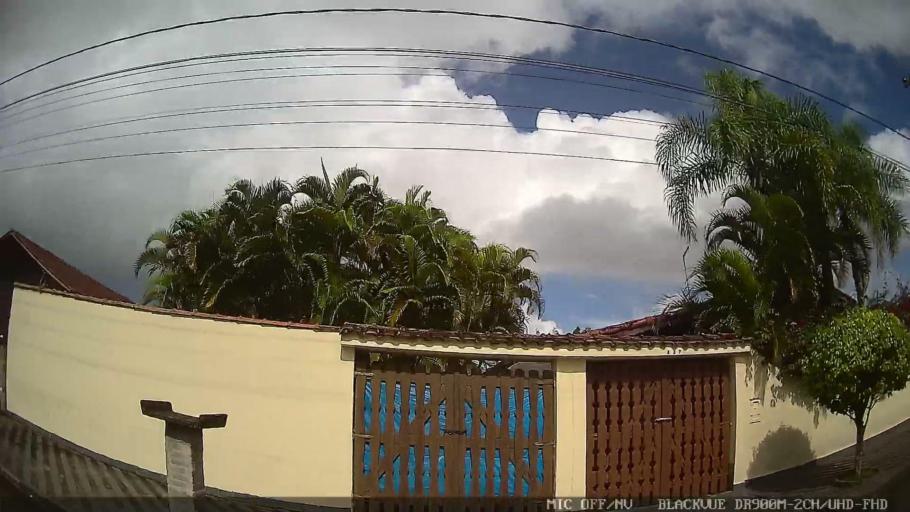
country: BR
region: Sao Paulo
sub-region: Itanhaem
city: Itanhaem
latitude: -24.2242
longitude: -46.8679
